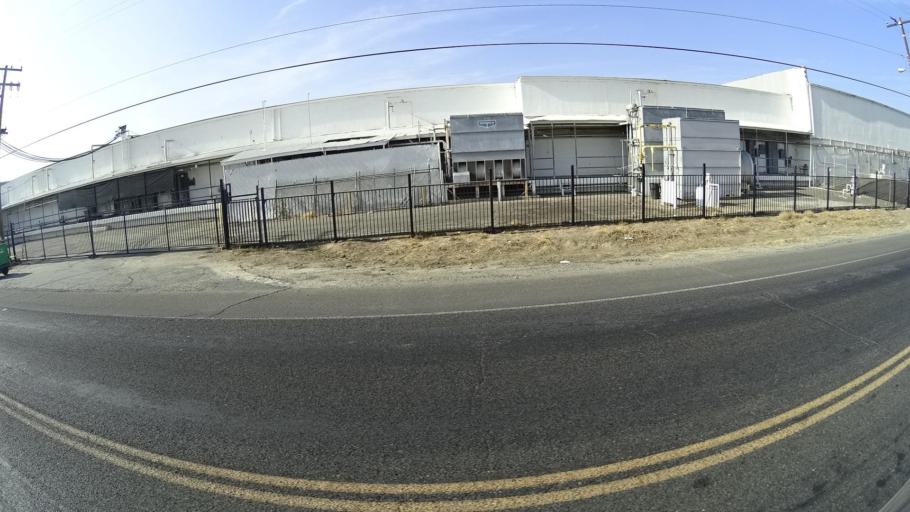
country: US
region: California
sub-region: Tulare County
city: Richgrove
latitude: 35.7413
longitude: -119.1451
